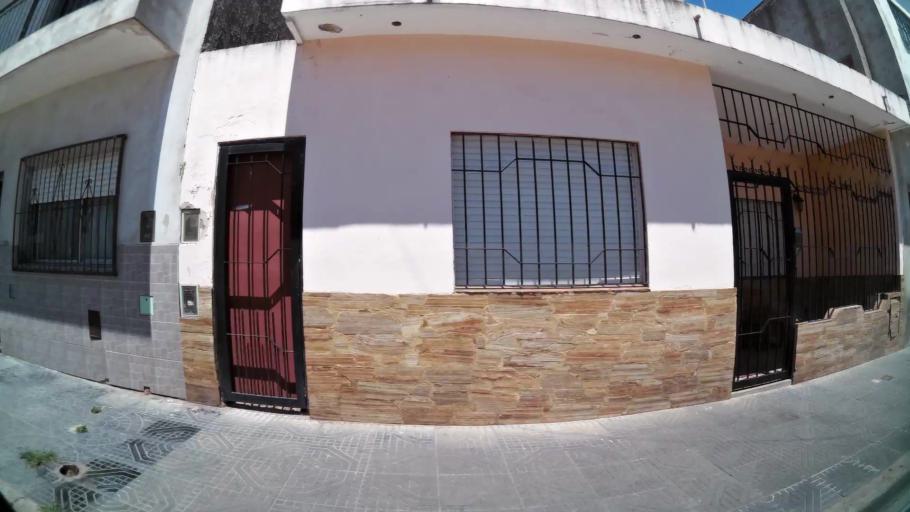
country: AR
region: Buenos Aires
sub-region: Partido de Avellaneda
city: Avellaneda
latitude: -34.6570
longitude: -58.4017
